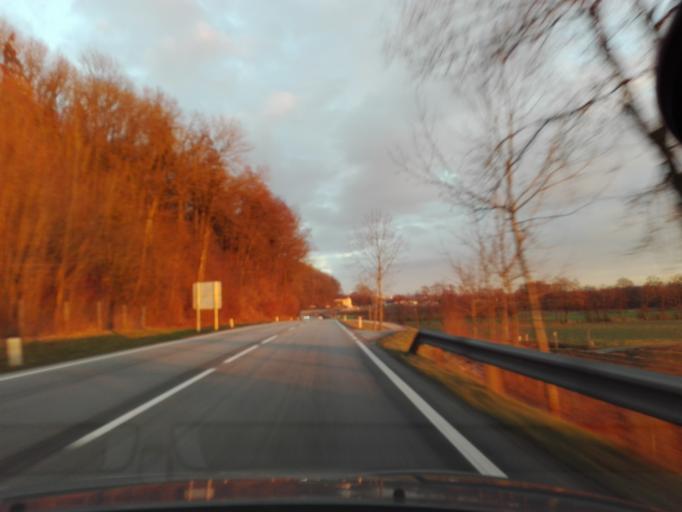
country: AT
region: Upper Austria
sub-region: Politischer Bezirk Perg
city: Perg
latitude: 48.2337
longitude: 14.6735
